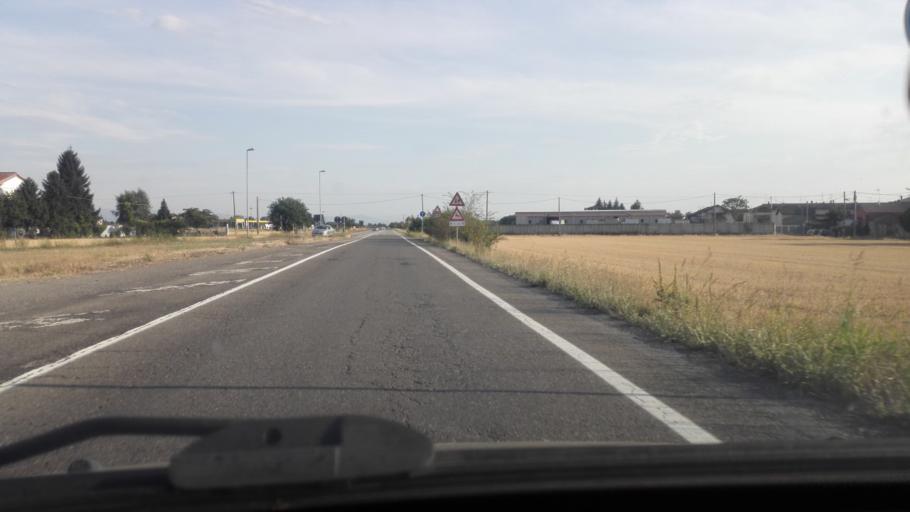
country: IT
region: Piedmont
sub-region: Provincia di Alessandria
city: Litta Parodi-Cascinagrossa
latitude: 44.8789
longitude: 8.6977
